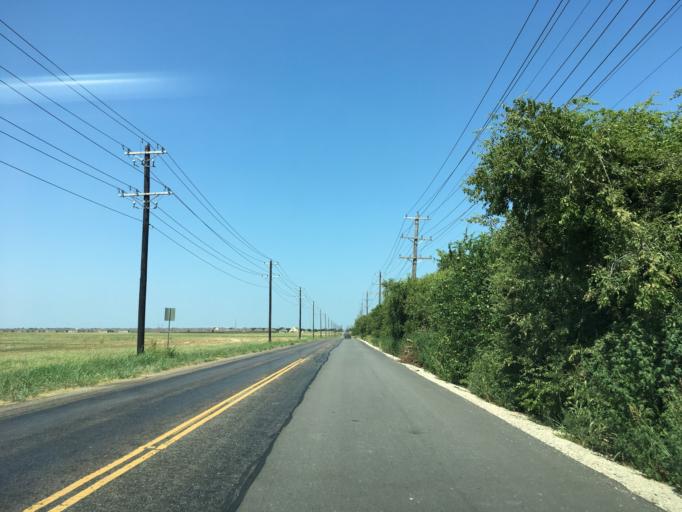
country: US
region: Texas
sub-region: Collin County
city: Prosper
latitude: 33.2038
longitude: -96.7702
